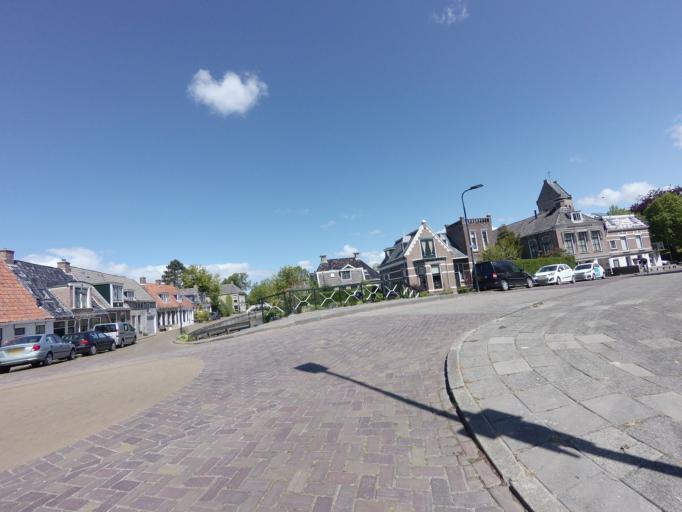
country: NL
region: Friesland
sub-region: Gemeente Harlingen
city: Harlingen
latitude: 53.1412
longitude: 5.4375
